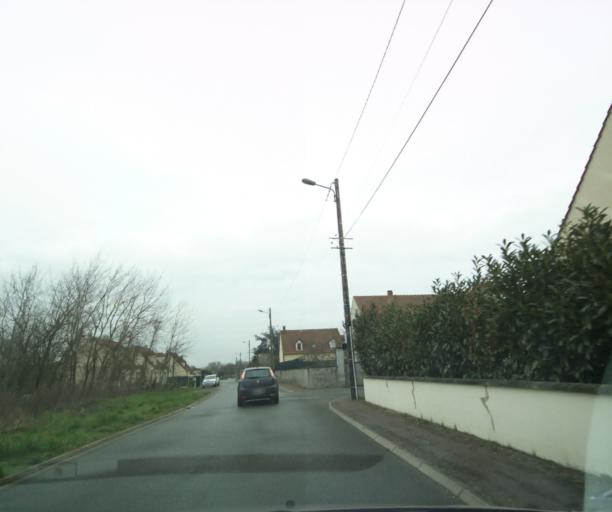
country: FR
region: Picardie
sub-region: Departement de l'Oise
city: Noyon
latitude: 49.5697
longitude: 3.0258
